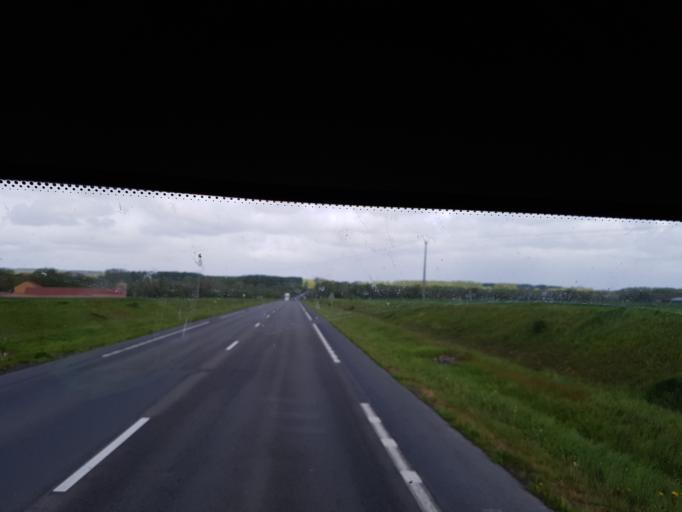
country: FR
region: Nord-Pas-de-Calais
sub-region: Departement du Nord
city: Proville
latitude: 50.1521
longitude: 3.1957
